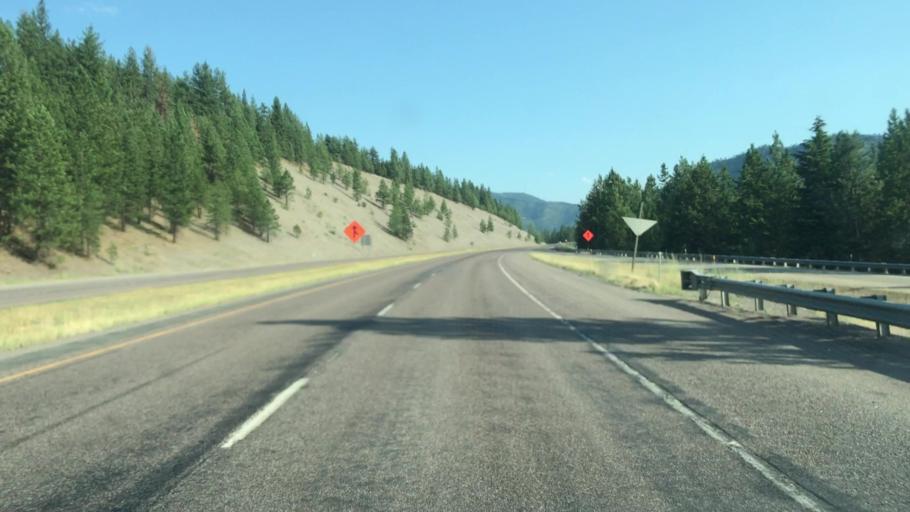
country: US
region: Montana
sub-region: Mineral County
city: Superior
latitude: 47.0242
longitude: -114.7382
